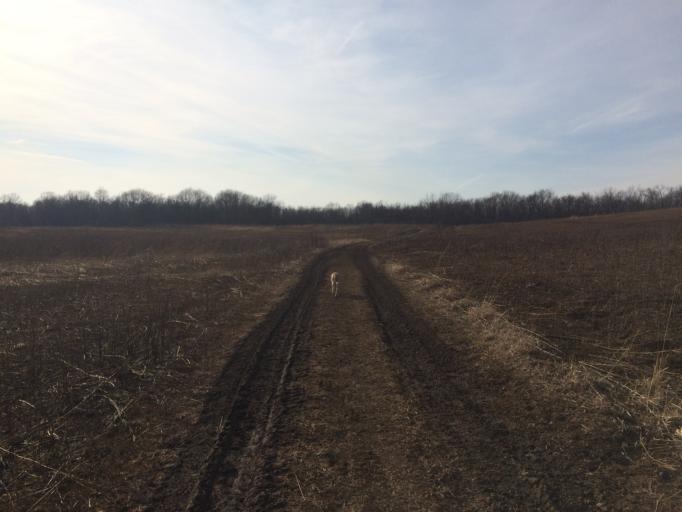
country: US
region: Illinois
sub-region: Cook County
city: Streamwood
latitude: 42.0586
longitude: -88.2008
